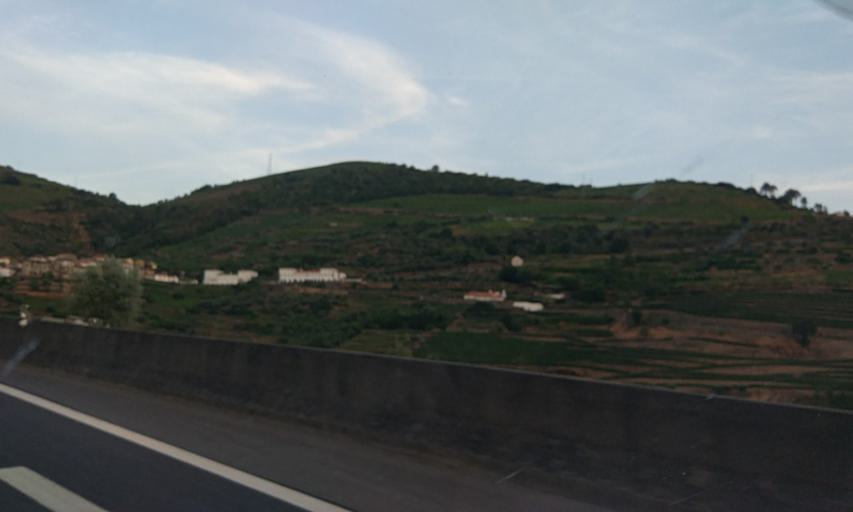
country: PT
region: Vila Real
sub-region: Peso da Regua
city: Peso da Regua
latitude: 41.1718
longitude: -7.7546
